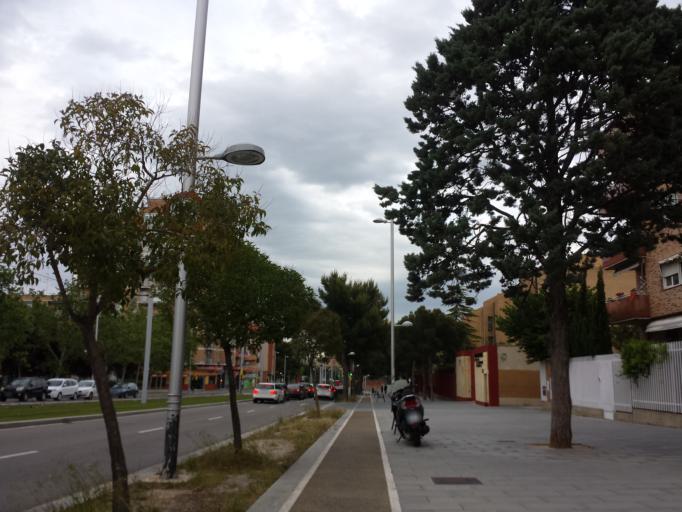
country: ES
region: Aragon
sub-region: Provincia de Zaragoza
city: Delicias
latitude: 41.6285
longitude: -0.9074
